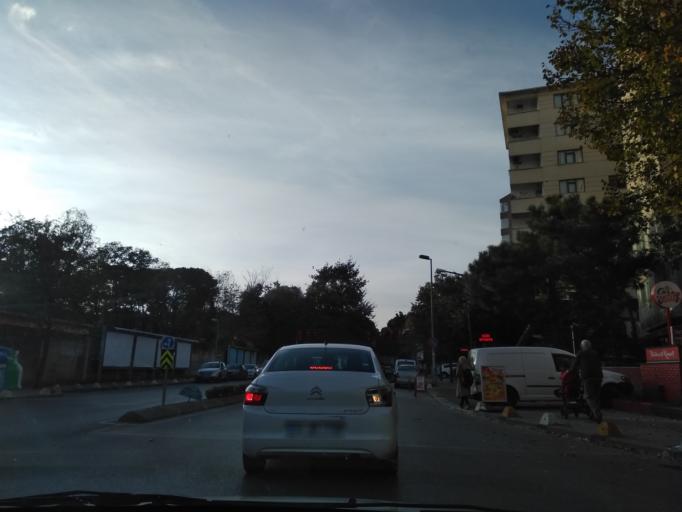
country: TR
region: Istanbul
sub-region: Atasehir
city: Atasehir
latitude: 40.9754
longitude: 29.0916
